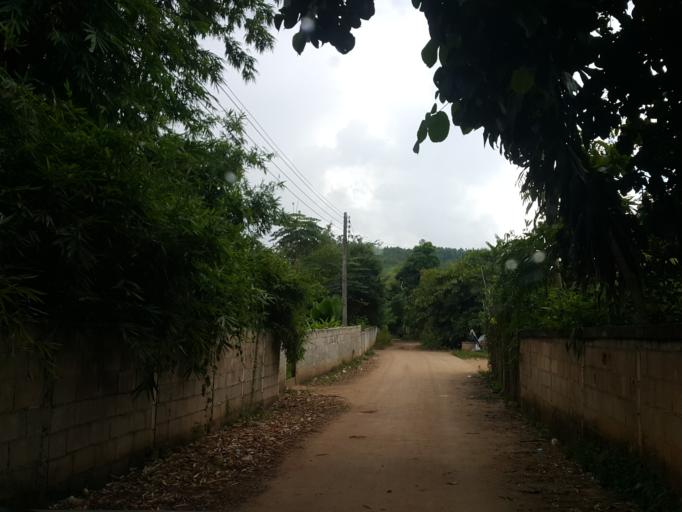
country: TH
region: Chiang Mai
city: Phrao
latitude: 19.3326
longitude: 99.1475
